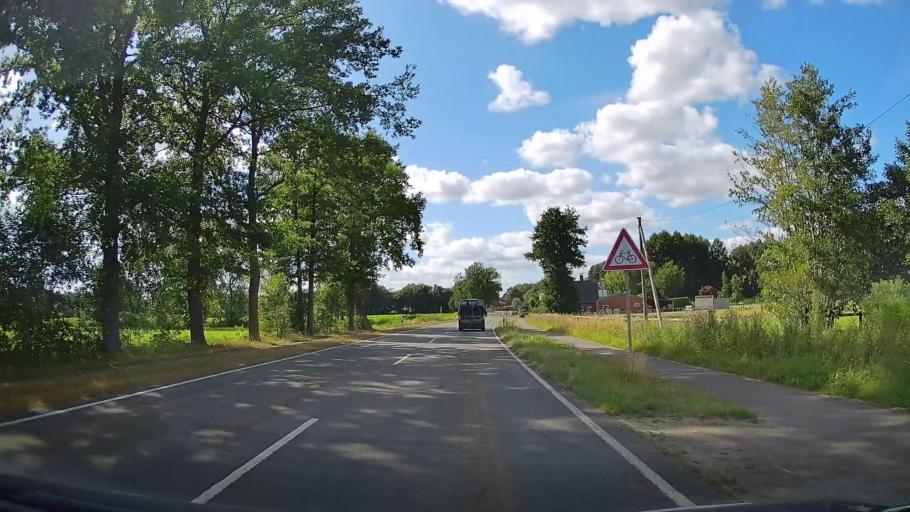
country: DE
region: Lower Saxony
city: Alfhausen
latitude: 52.5002
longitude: 7.9726
